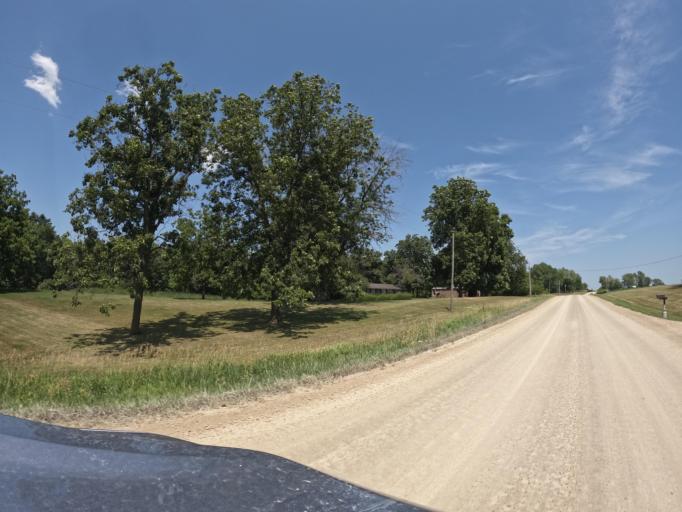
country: US
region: Iowa
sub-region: Henry County
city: Mount Pleasant
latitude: 40.9467
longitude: -91.6069
